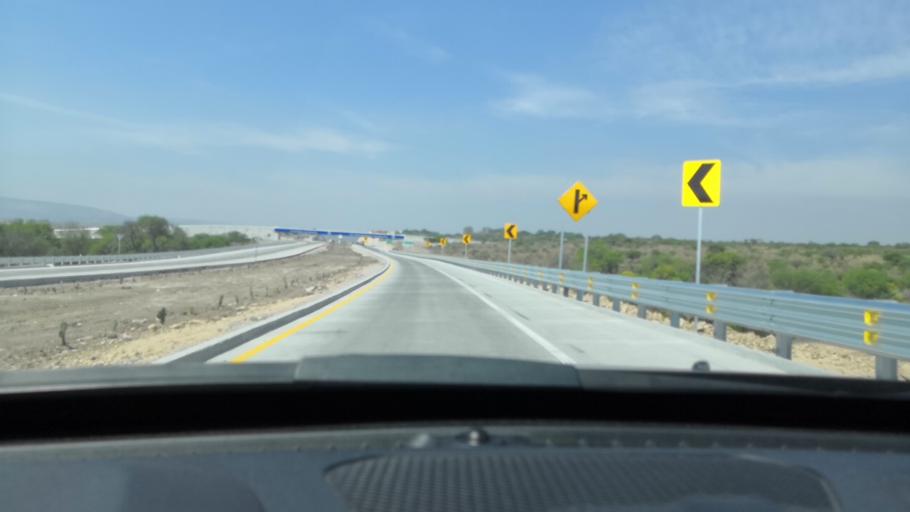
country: MX
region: Guanajuato
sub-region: Purisima del Rincon
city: Potrerillos (Guanajal)
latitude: 21.0871
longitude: -101.8207
